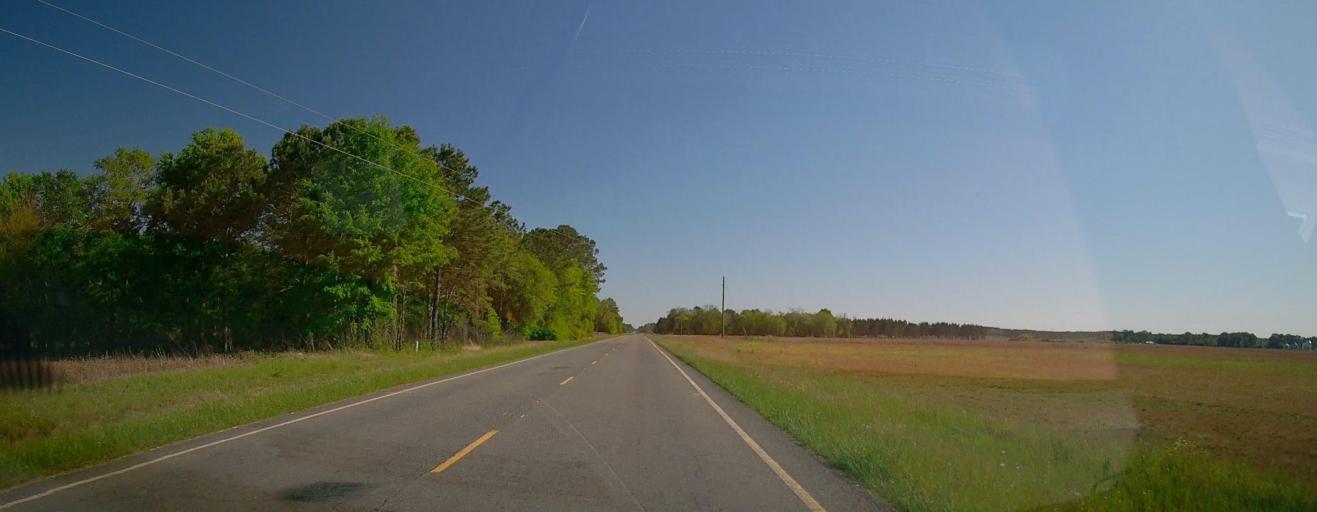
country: US
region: Georgia
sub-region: Wilcox County
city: Rochelle
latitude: 32.0829
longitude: -83.5034
